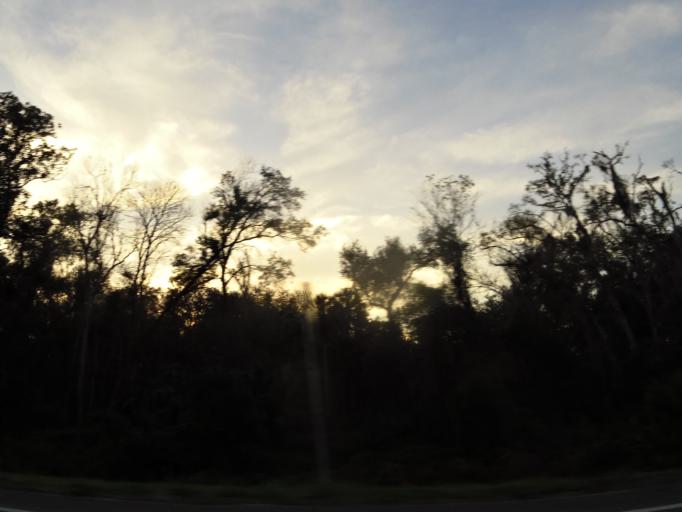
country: US
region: Florida
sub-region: Volusia County
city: North DeLand
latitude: 29.1071
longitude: -81.2946
